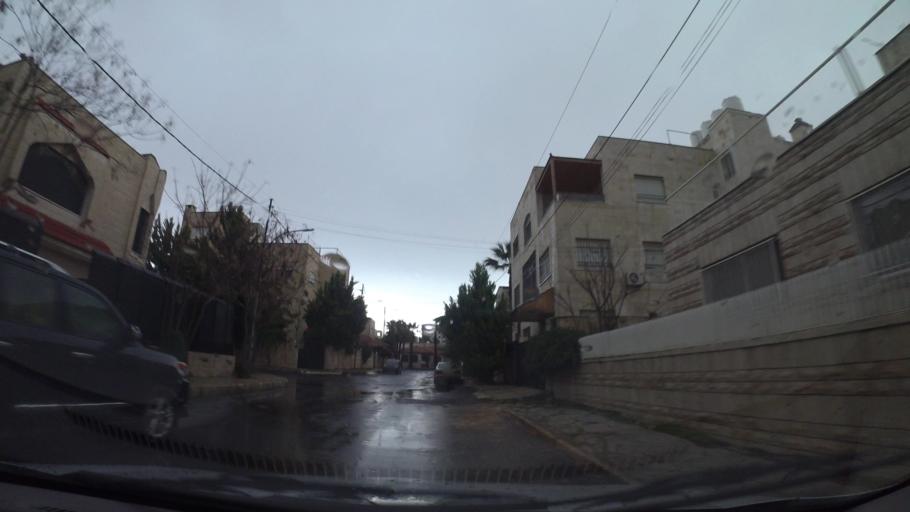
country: JO
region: Amman
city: Umm as Summaq
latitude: 31.8991
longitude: 35.8553
